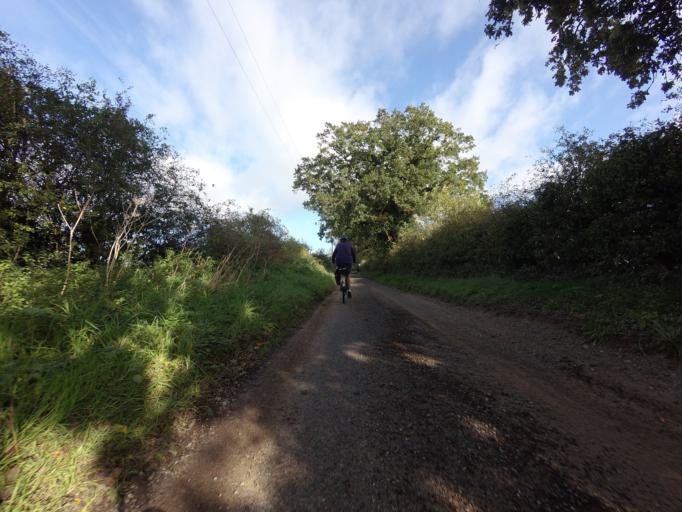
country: GB
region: England
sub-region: Norfolk
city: Dersingham
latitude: 52.8628
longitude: 0.6662
